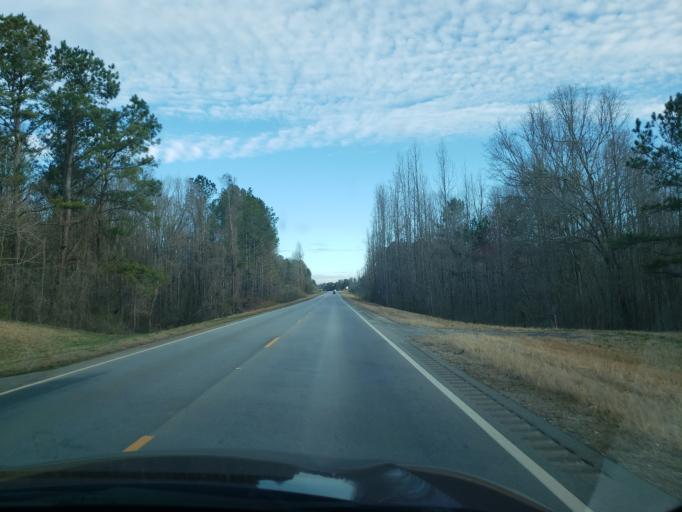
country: US
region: Alabama
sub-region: Randolph County
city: Wedowee
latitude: 33.4186
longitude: -85.5489
